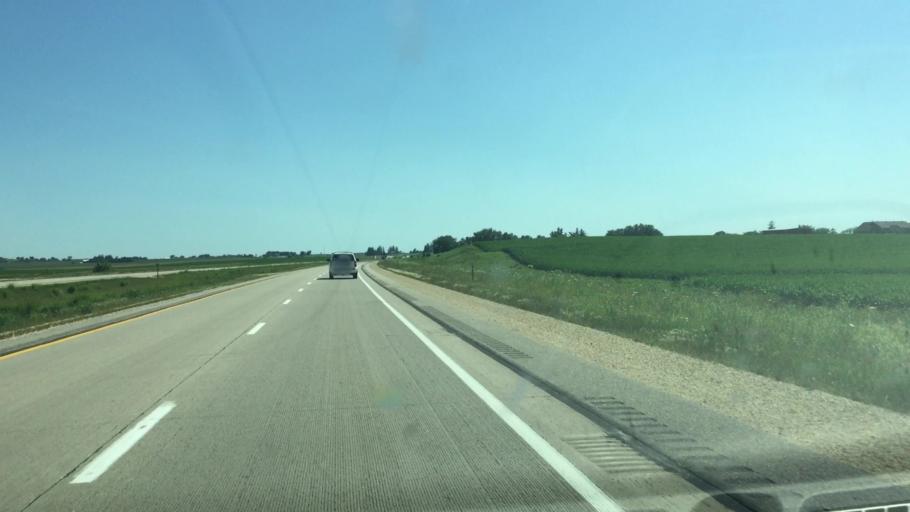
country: US
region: Iowa
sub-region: Jones County
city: Monticello
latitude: 42.1912
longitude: -91.2169
